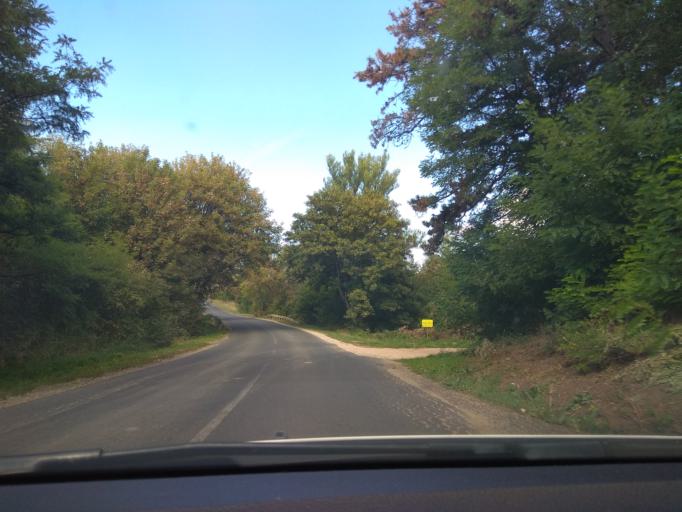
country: HU
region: Borsod-Abauj-Zemplen
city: Tallya
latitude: 48.2165
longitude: 21.2441
